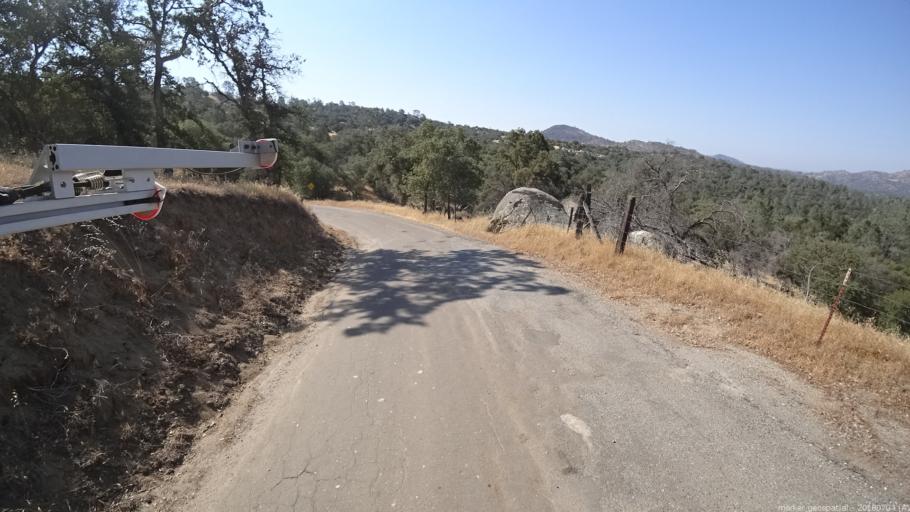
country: US
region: California
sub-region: Fresno County
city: Auberry
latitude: 37.1032
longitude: -119.6235
